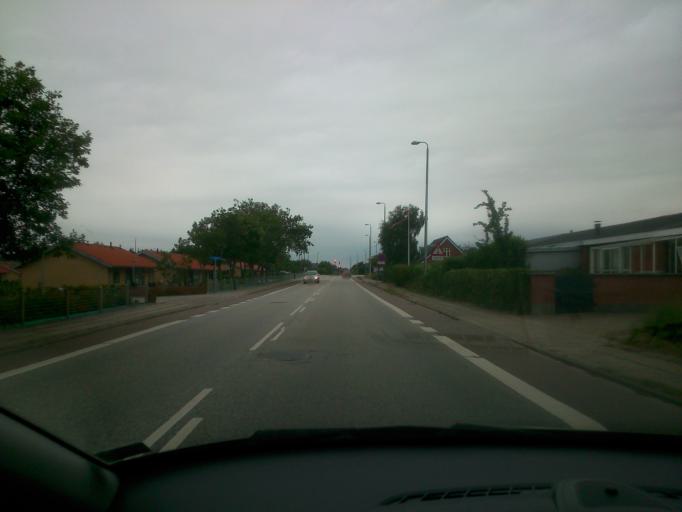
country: DK
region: Central Jutland
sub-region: Ringkobing-Skjern Kommune
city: Skjern
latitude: 55.9534
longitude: 8.4869
